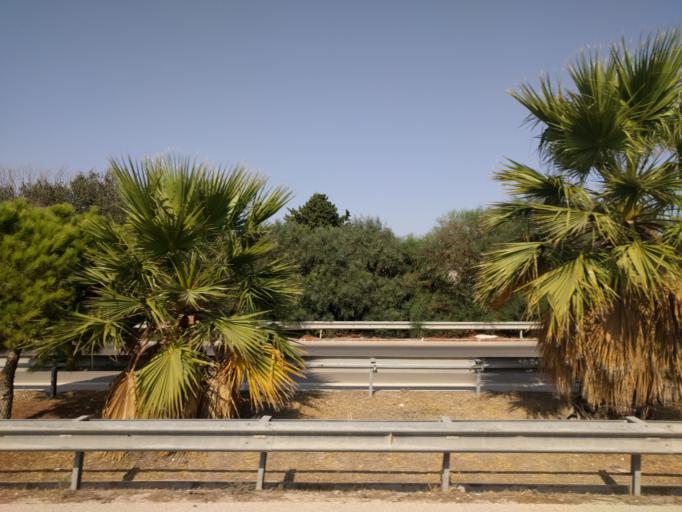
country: TR
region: Izmir
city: Alacati
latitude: 38.2862
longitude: 26.3838
